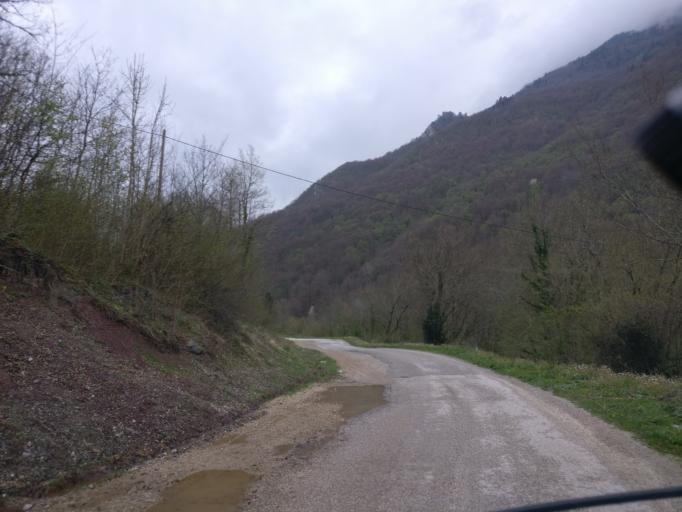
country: BA
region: Republika Srpska
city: Foca
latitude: 43.3528
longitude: 18.8268
